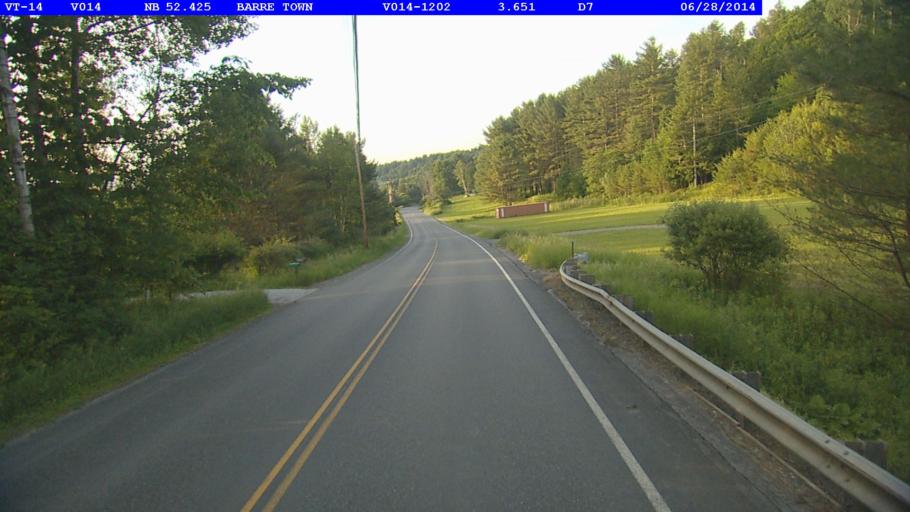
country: US
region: Vermont
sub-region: Washington County
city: Barre
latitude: 44.2303
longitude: -72.4893
